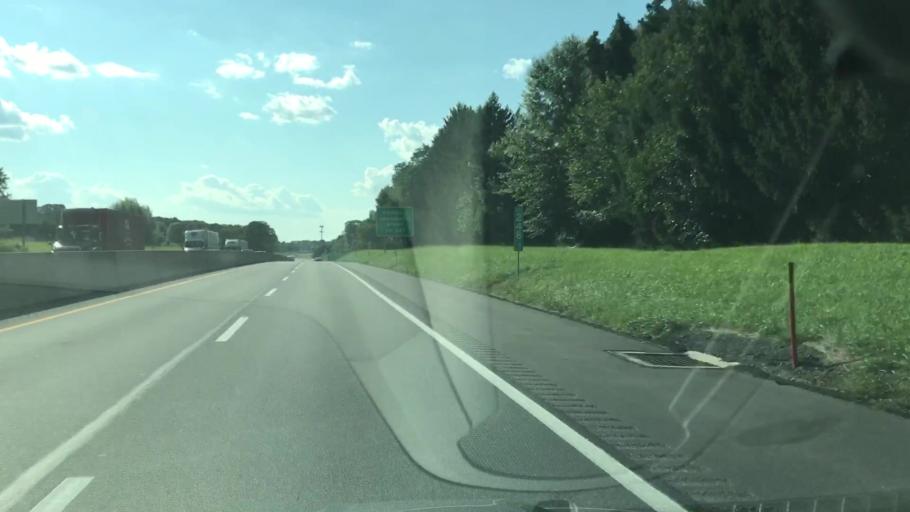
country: US
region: Pennsylvania
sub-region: Dauphin County
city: Highspire
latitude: 40.2138
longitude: -76.7724
